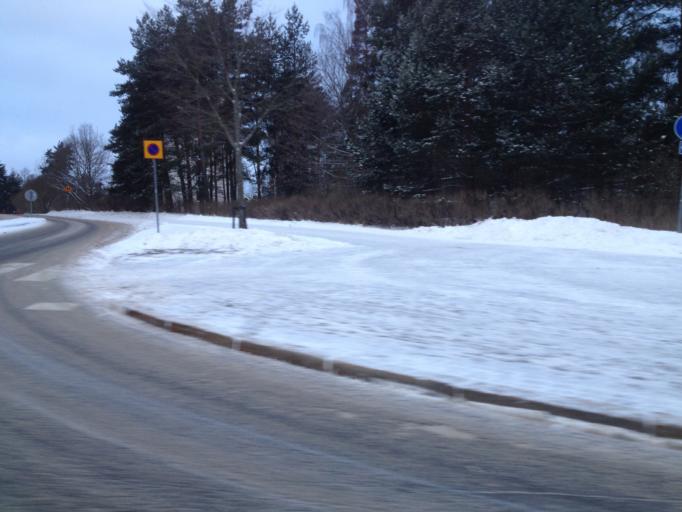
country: FI
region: Uusimaa
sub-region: Helsinki
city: Vantaa
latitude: 60.2102
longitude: 25.1490
